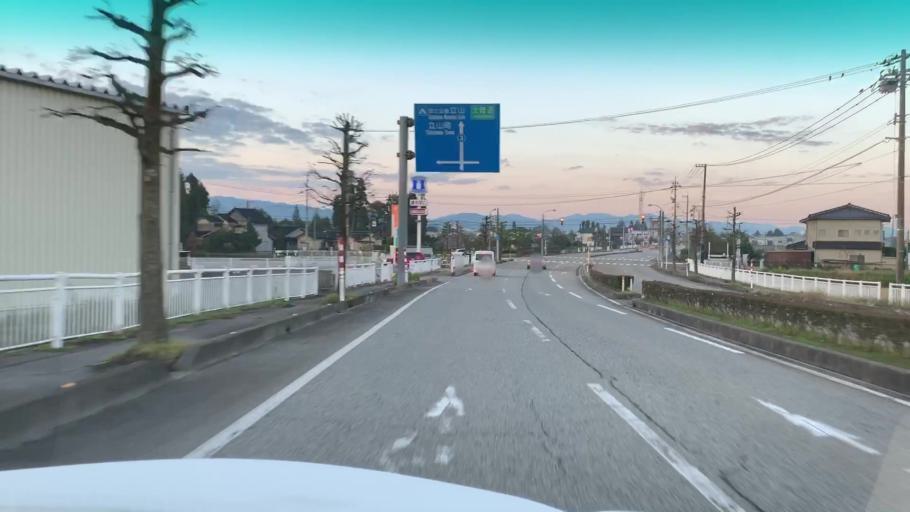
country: JP
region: Toyama
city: Kamiichi
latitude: 36.6929
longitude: 137.3425
